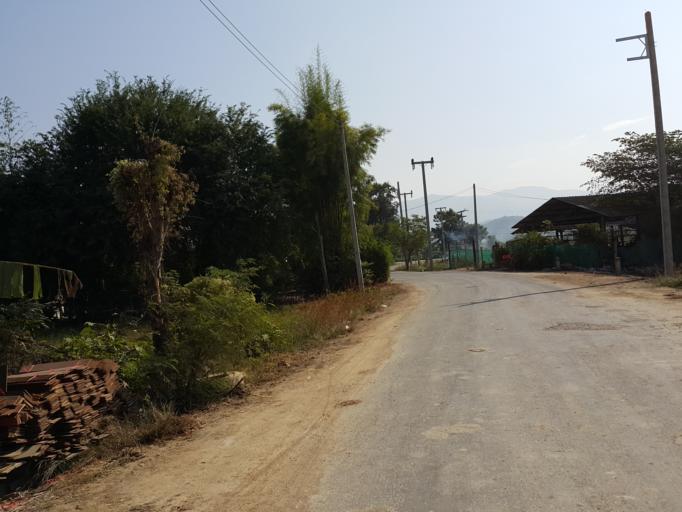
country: TH
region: Lamphun
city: Ban Thi
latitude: 18.6827
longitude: 99.1362
